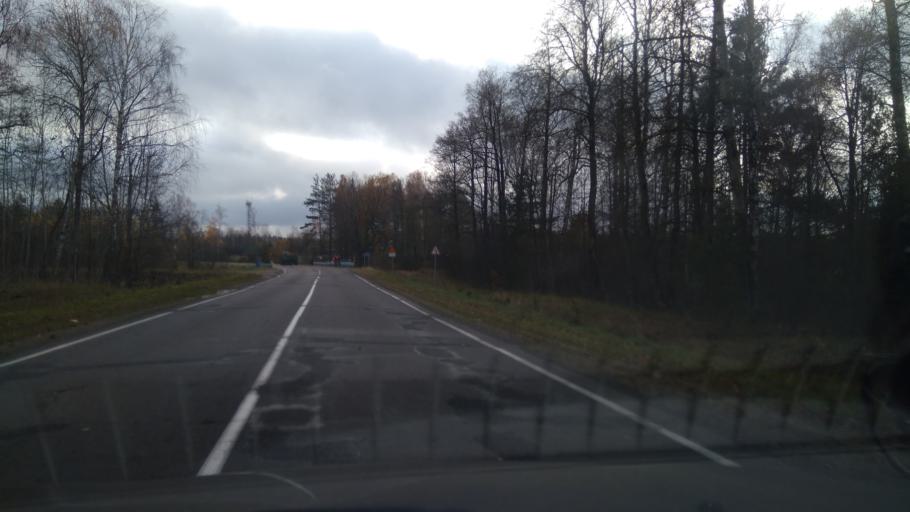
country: BY
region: Minsk
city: Slutsk
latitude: 53.2086
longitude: 27.7640
